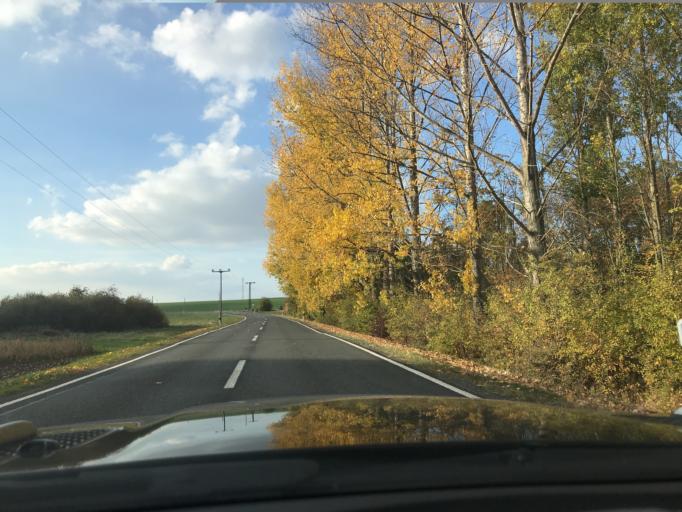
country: DE
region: Thuringia
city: Schonstedt
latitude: 51.1193
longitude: 10.5703
